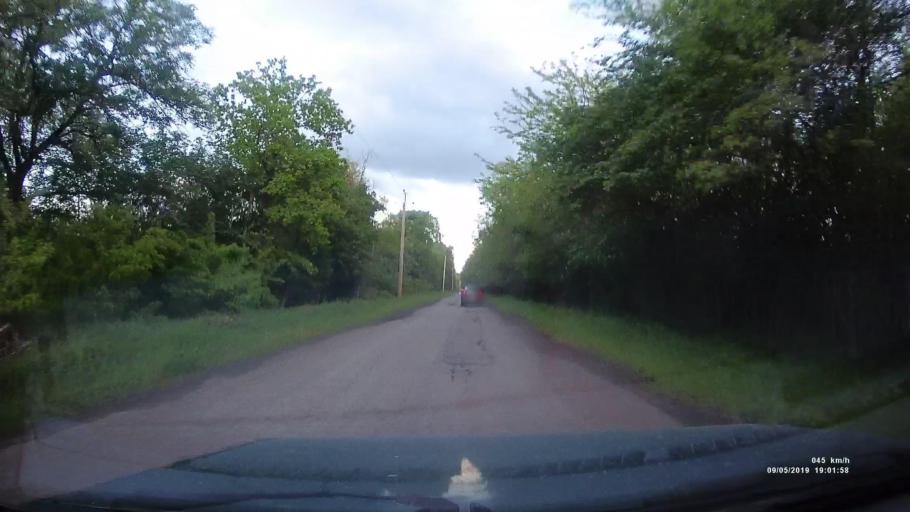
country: RU
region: Krasnodarskiy
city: Kanelovskaya
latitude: 46.7465
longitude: 39.1484
